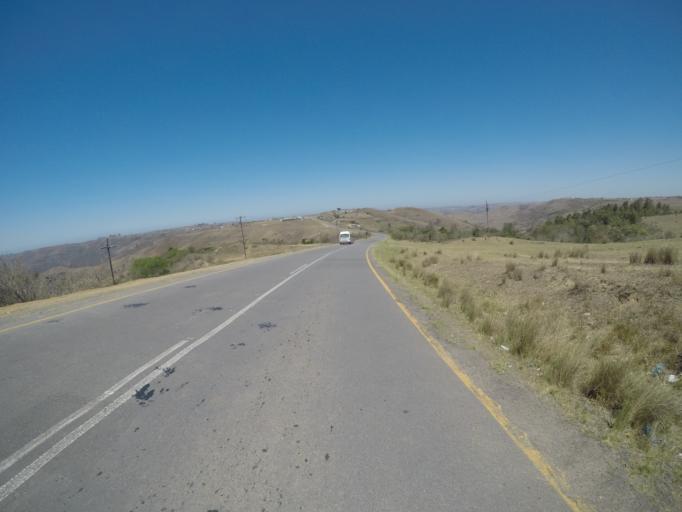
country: ZA
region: Eastern Cape
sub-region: OR Tambo District Municipality
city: Mthatha
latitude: -31.8995
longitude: 28.9458
